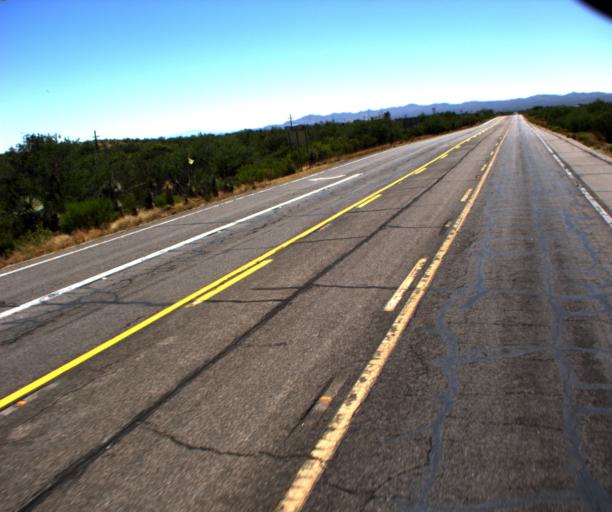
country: US
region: Arizona
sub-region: Pinal County
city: Oracle
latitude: 32.6207
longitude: -110.8030
